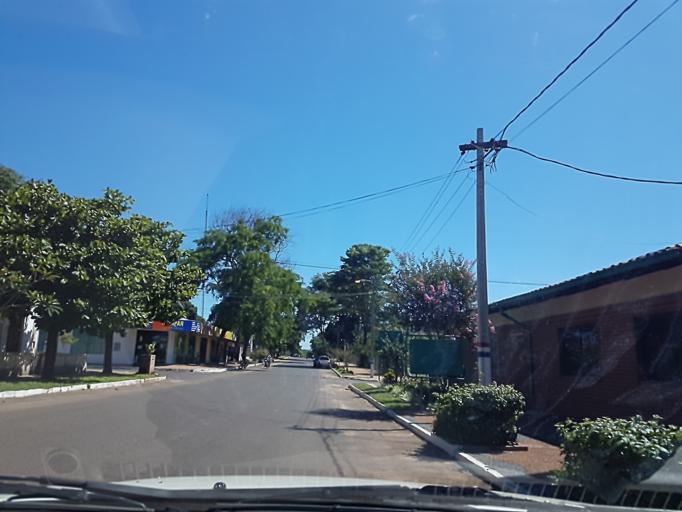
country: PY
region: Cordillera
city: Atyra
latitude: -25.2781
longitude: -57.1721
